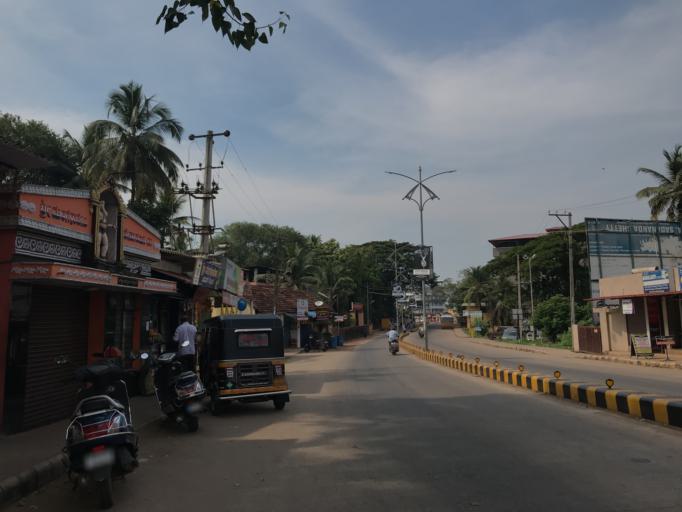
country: IN
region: Karnataka
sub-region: Dakshina Kannada
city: Ullal
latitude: 12.8494
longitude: 74.8458
